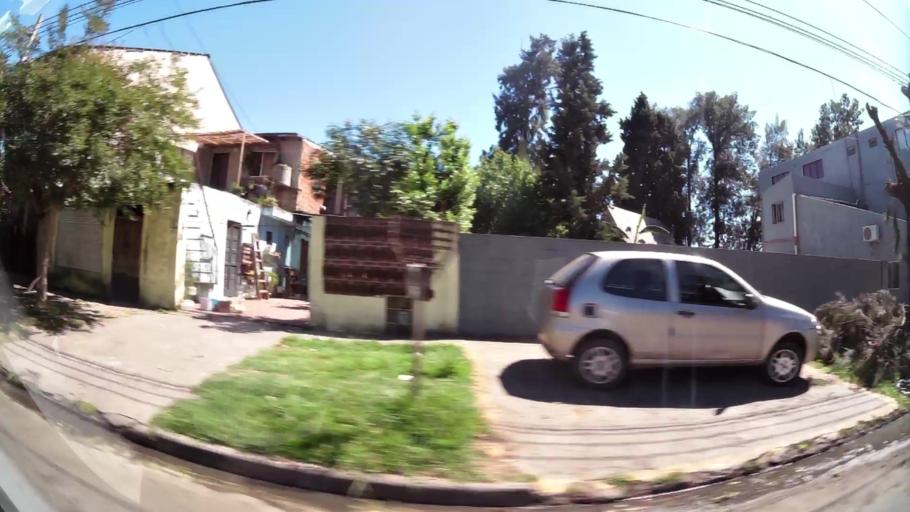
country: AR
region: Buenos Aires
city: Hurlingham
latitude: -34.5032
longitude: -58.6303
